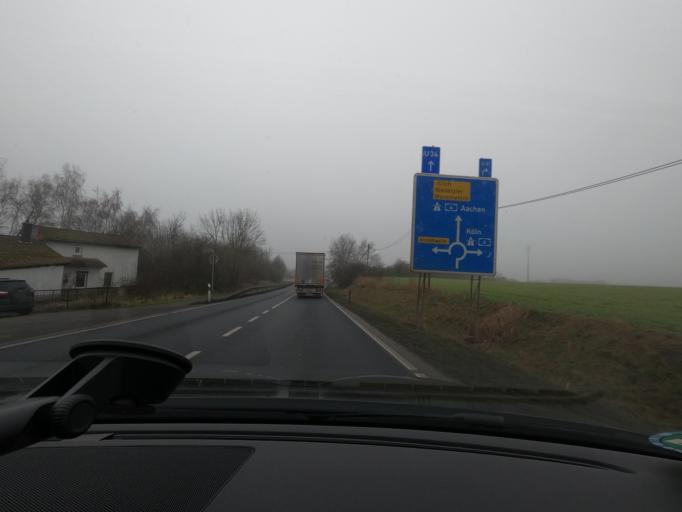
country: DE
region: North Rhine-Westphalia
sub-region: Regierungsbezirk Koln
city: Merzenich
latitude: 50.8424
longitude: 6.5184
